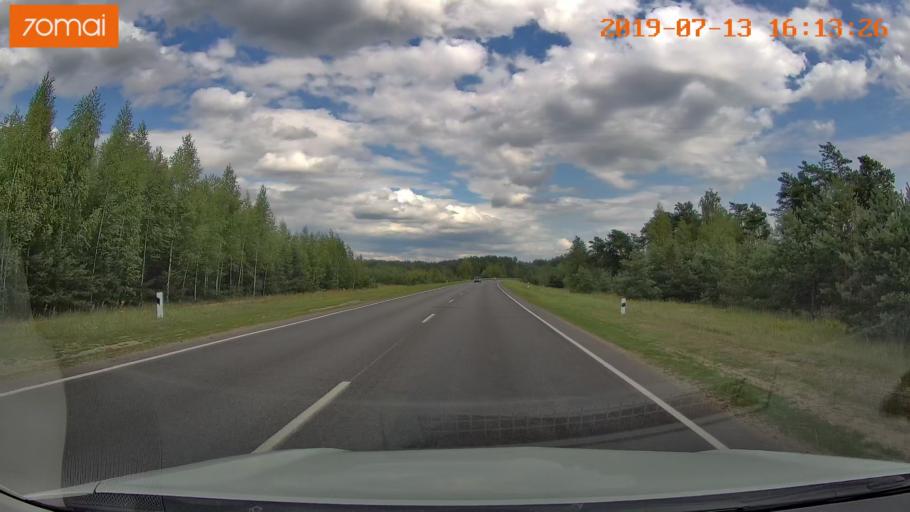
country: BY
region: Mogilev
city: Babruysk
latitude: 53.1629
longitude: 29.3034
